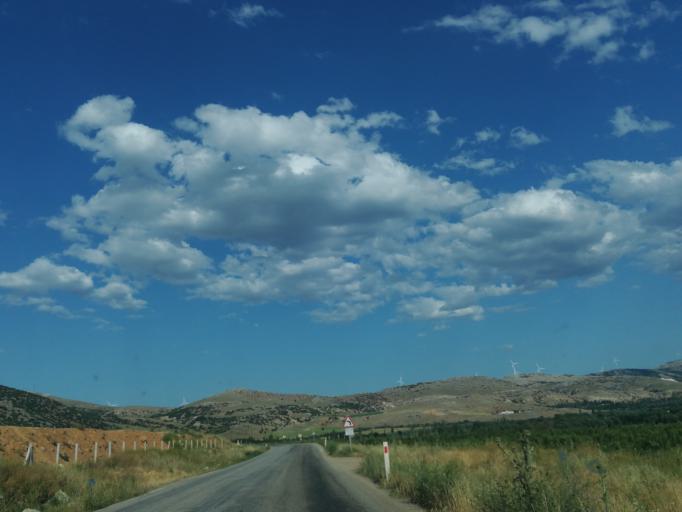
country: TR
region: Afyonkarahisar
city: Dinar
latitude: 38.0991
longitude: 30.1425
